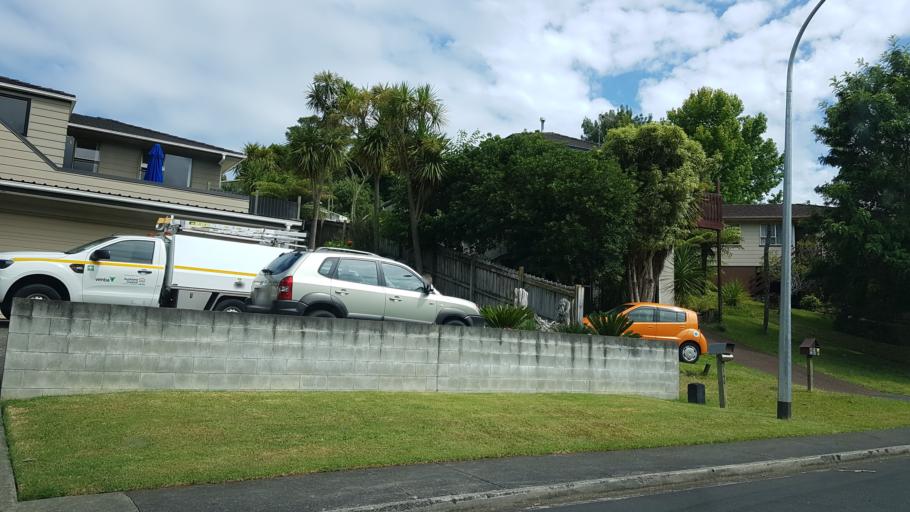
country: NZ
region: Auckland
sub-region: Auckland
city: North Shore
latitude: -36.7701
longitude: 174.7061
